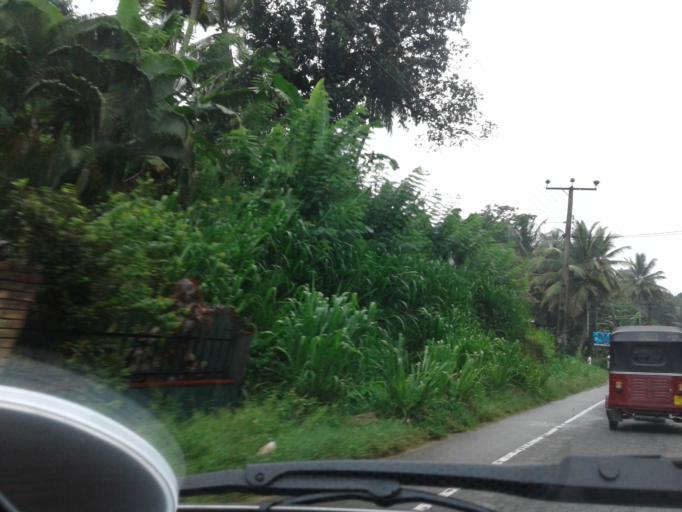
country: LK
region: Central
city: Kadugannawa
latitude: 7.2339
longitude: 80.2583
